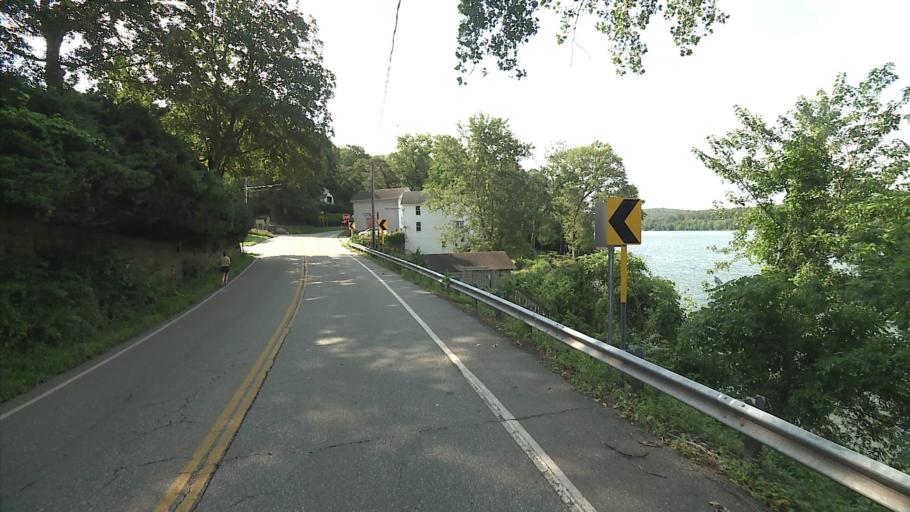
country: US
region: Connecticut
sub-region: Middlesex County
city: East Haddam
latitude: 41.4638
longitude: -72.4647
